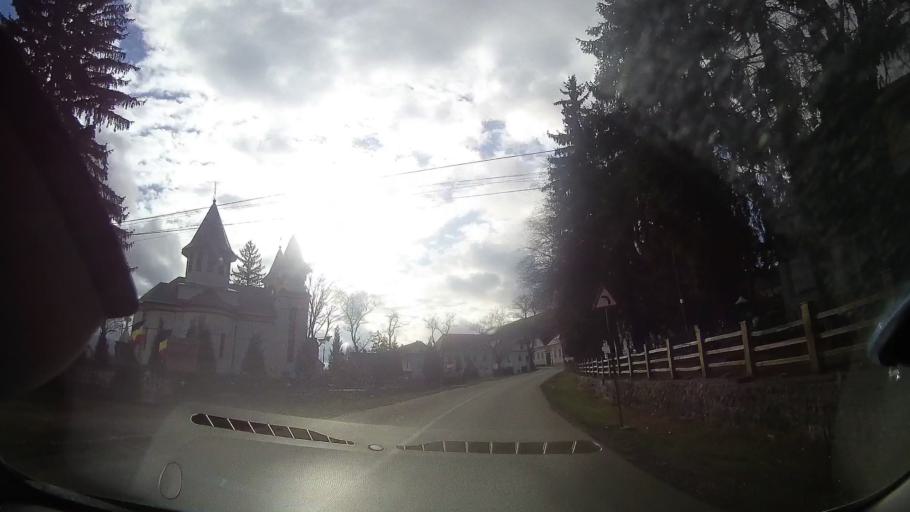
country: RO
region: Alba
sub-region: Comuna Rimetea
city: Rimetea
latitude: 46.4524
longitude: 23.5678
